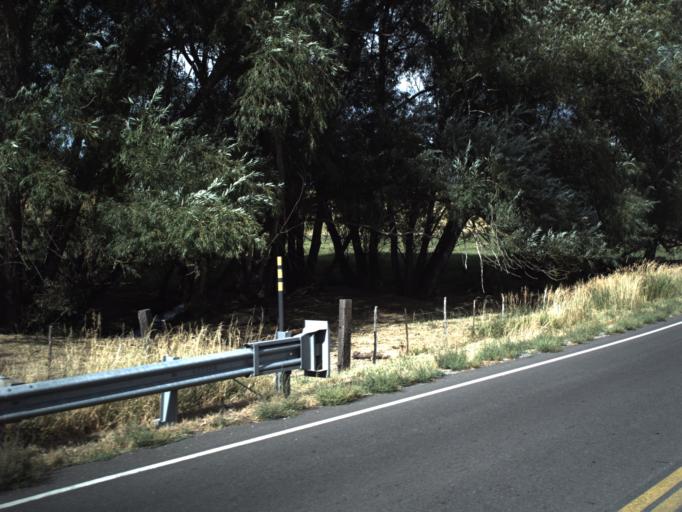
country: US
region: Utah
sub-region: Cache County
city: Wellsville
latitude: 41.6389
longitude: -111.9244
